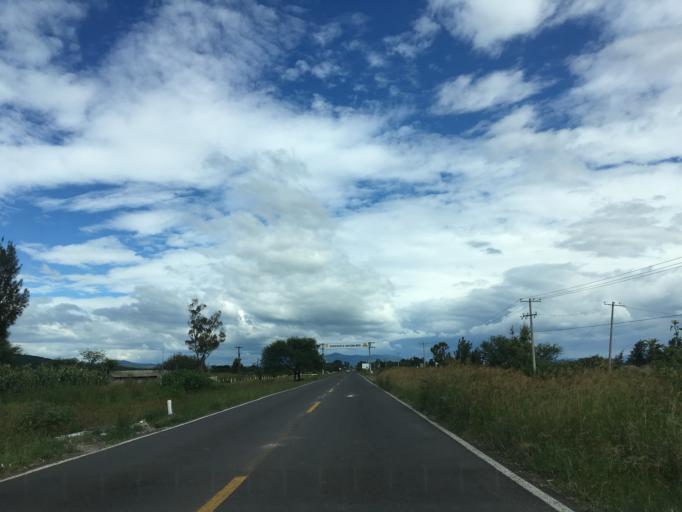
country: MX
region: Michoacan
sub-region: Cuitzeo
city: Cuamio
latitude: 20.0748
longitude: -101.1295
